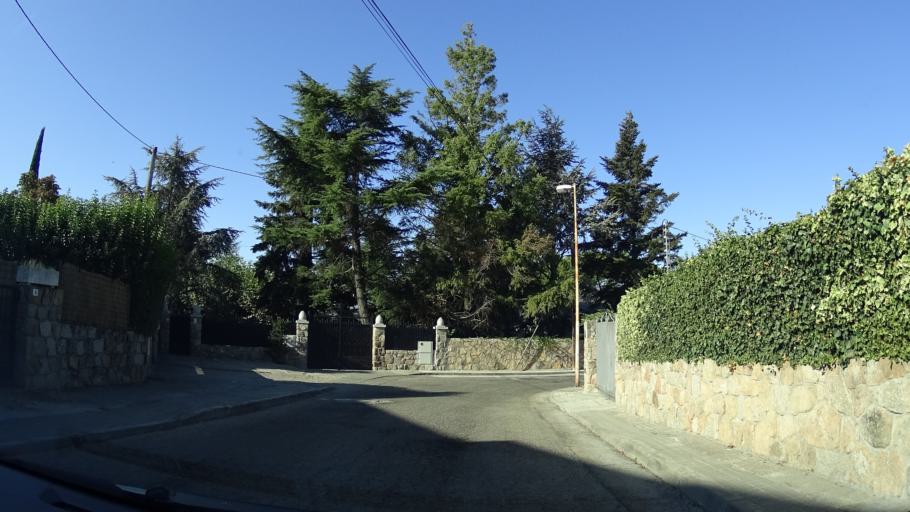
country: ES
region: Madrid
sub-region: Provincia de Madrid
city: Colmenarejo
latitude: 40.5593
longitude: -4.0202
